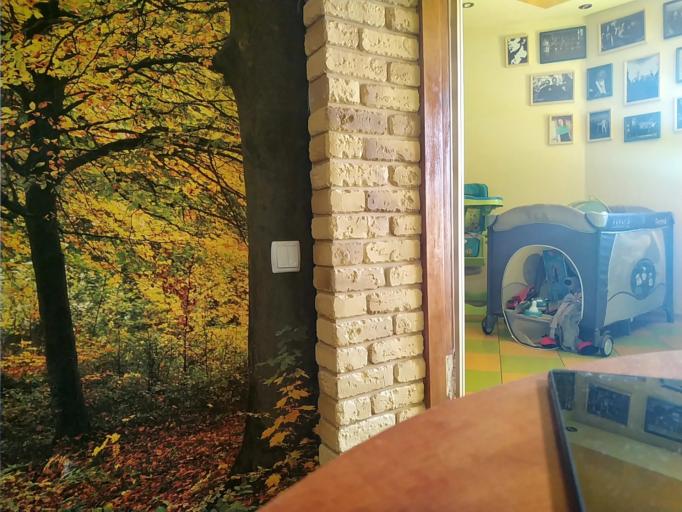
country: RU
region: Tverskaya
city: Vyshniy Volochek
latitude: 57.5274
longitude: 34.6186
